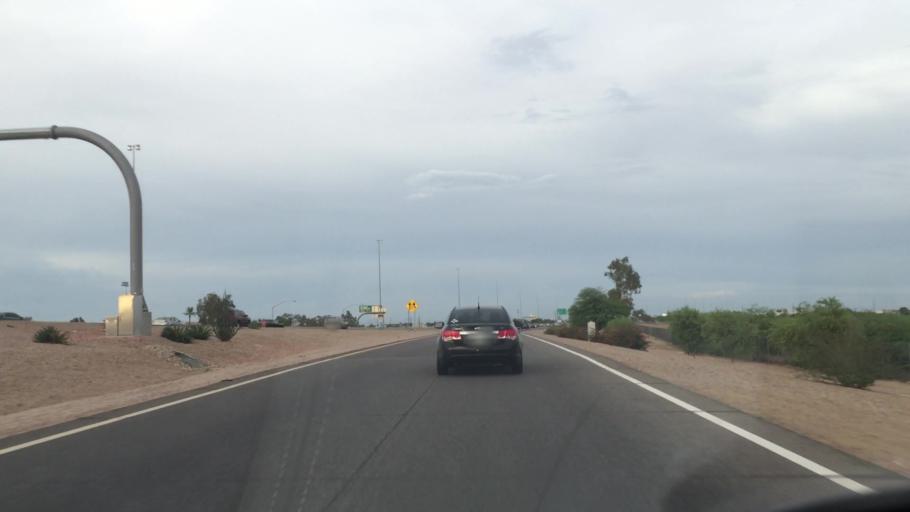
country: US
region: Arizona
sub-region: Maricopa County
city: Tolleson
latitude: 33.4592
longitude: -112.3044
